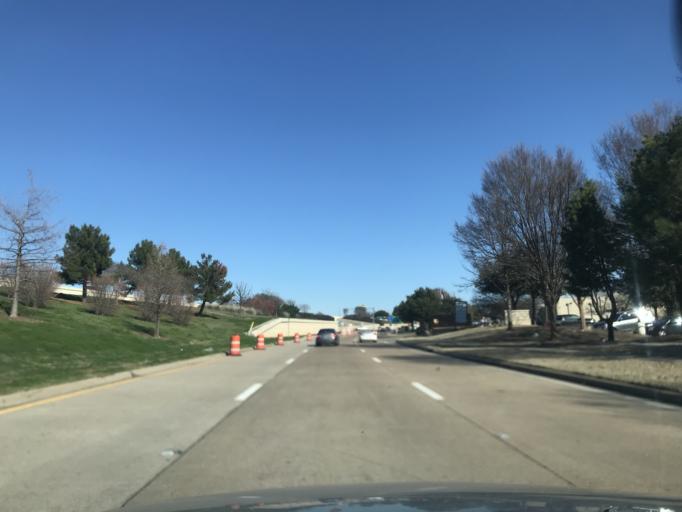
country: US
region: Texas
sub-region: Dallas County
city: Coppell
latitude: 32.9912
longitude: -96.9770
